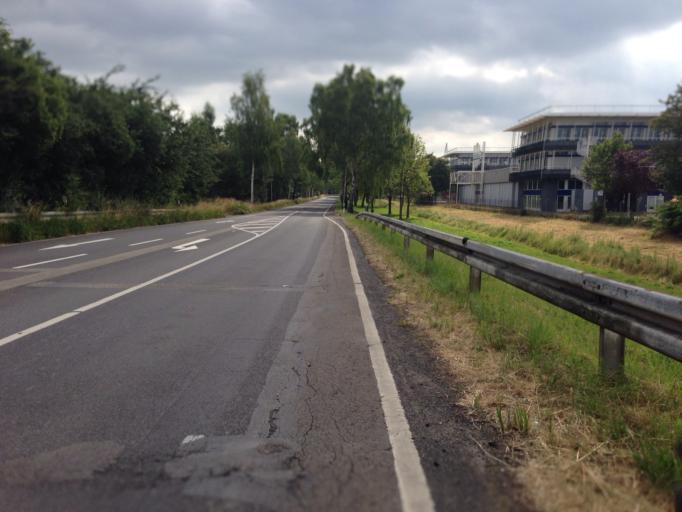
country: DE
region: Hesse
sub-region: Regierungsbezirk Darmstadt
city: Hanau am Main
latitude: 50.1531
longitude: 8.9268
